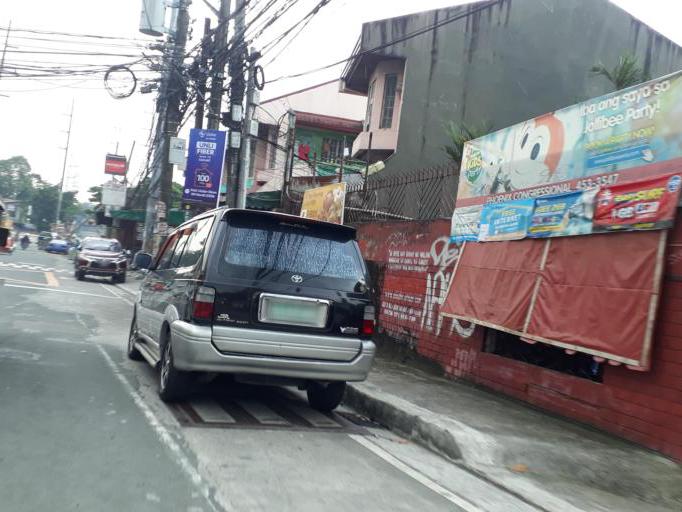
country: PH
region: Calabarzon
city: Bagong Pagasa
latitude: 14.6720
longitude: 121.0507
